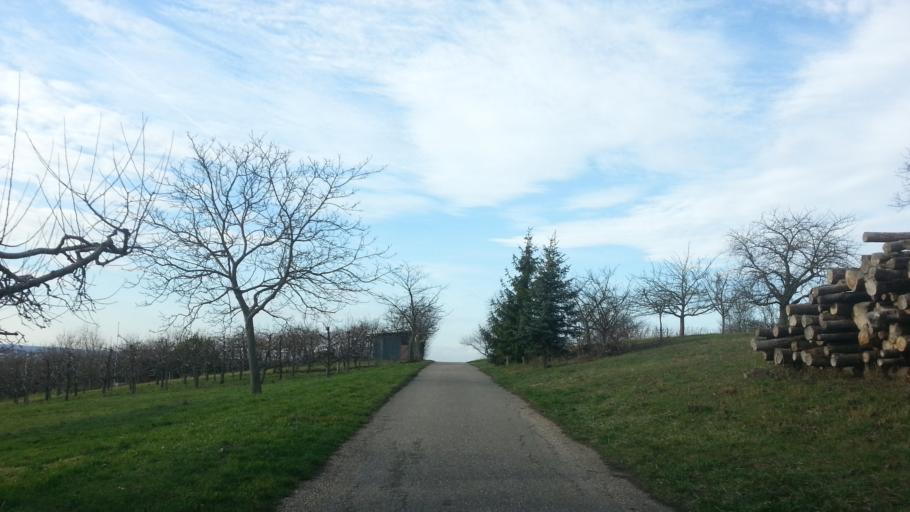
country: DE
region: Baden-Wuerttemberg
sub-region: Karlsruhe Region
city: Ubstadt-Weiher
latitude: 49.1834
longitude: 8.6653
